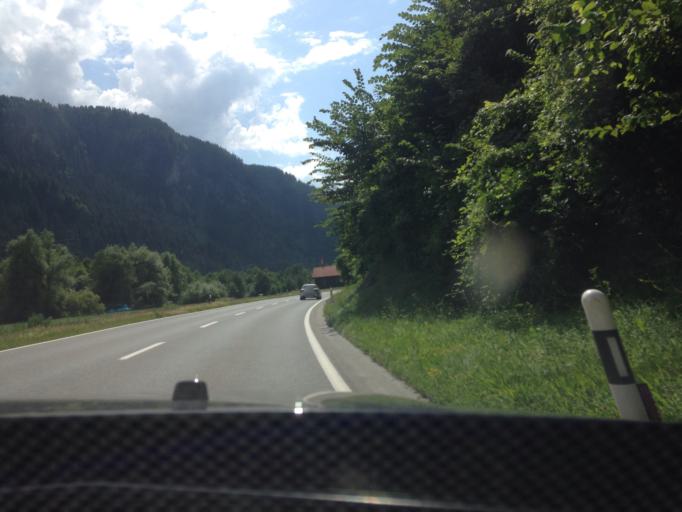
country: CH
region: Grisons
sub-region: Surselva District
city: Breil
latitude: 46.7621
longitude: 9.0957
